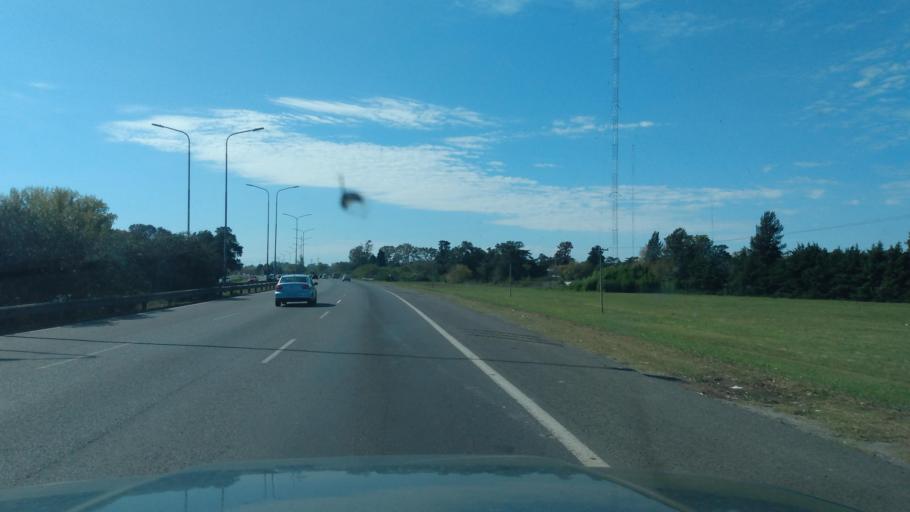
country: AR
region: Buenos Aires
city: Hurlingham
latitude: -34.6023
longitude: -58.7016
